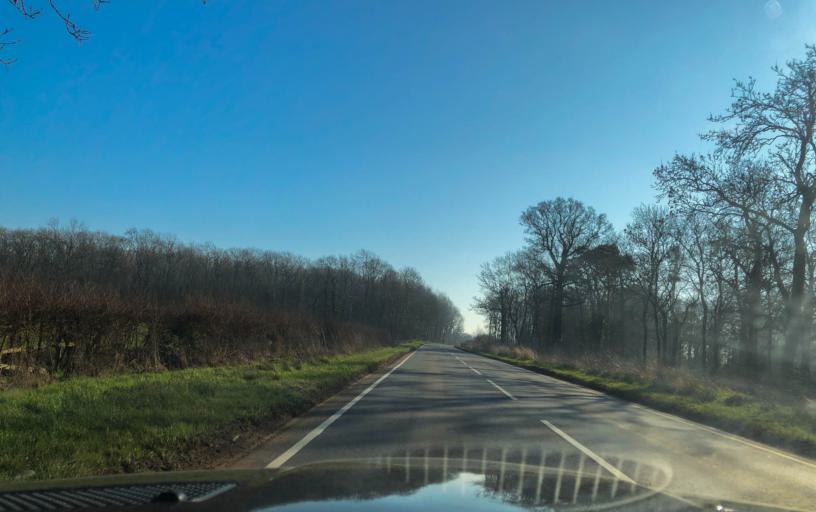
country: GB
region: England
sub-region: Warwickshire
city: Wellesbourne Mountford
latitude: 52.1765
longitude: -1.5628
